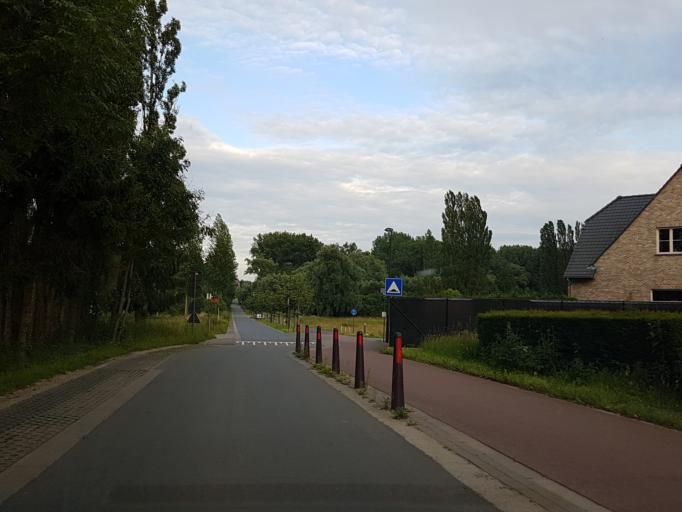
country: BE
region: Flanders
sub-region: Provincie Oost-Vlaanderen
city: Denderleeuw
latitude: 50.9293
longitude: 4.1046
